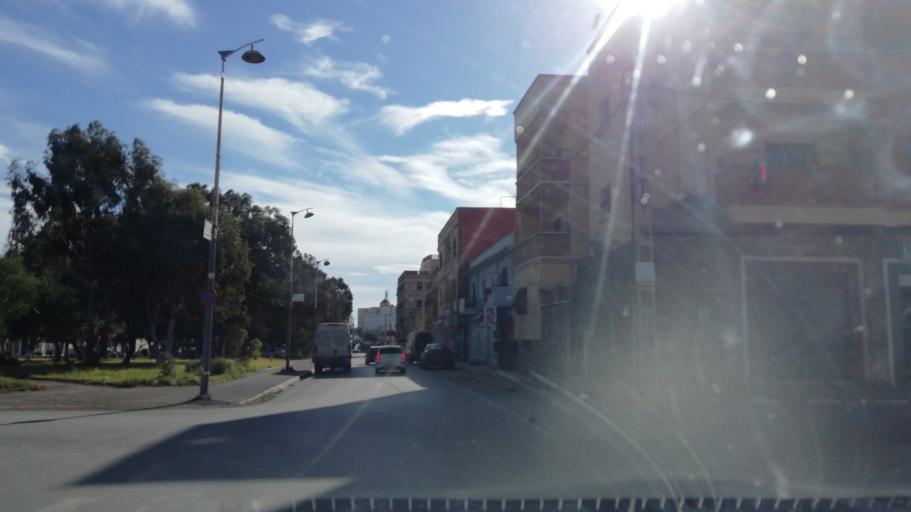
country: DZ
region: Oran
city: Oran
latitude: 35.6962
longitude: -0.6195
